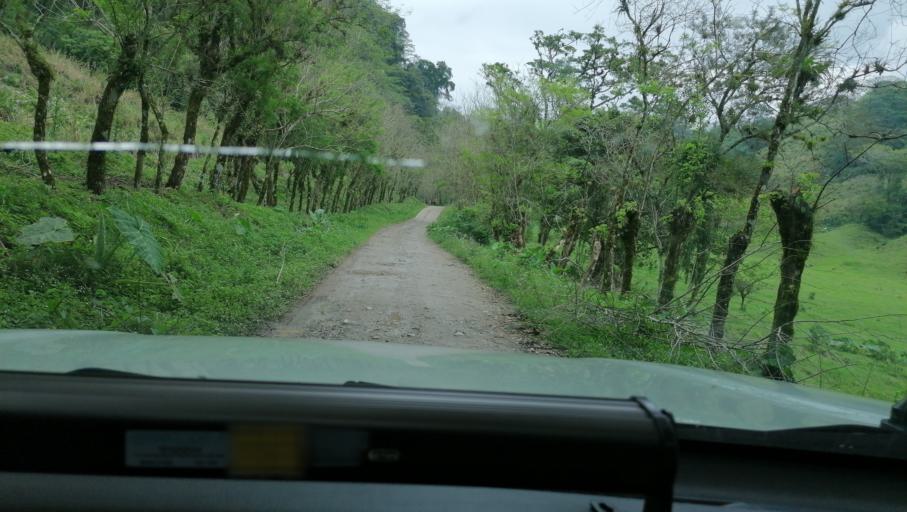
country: MX
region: Chiapas
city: Ixtacomitan
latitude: 17.3525
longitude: -93.1501
